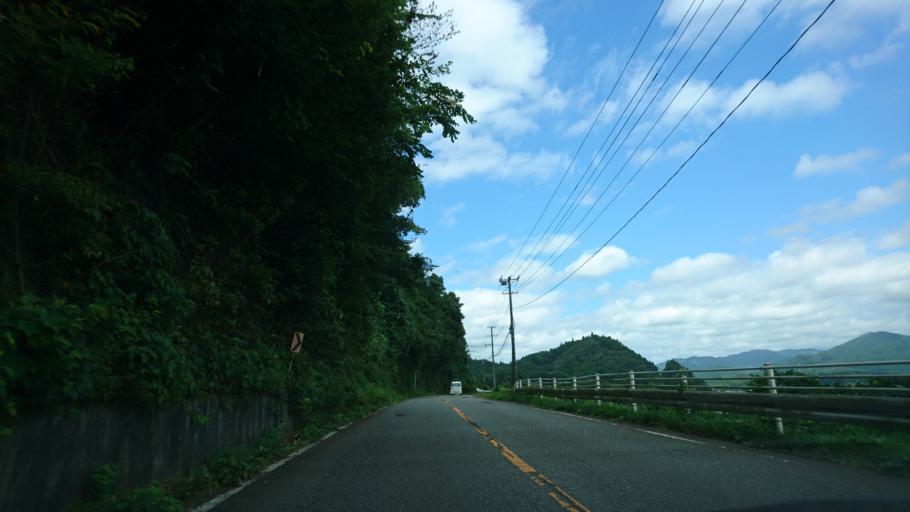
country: JP
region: Miyagi
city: Furukawa
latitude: 38.7763
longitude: 140.8553
